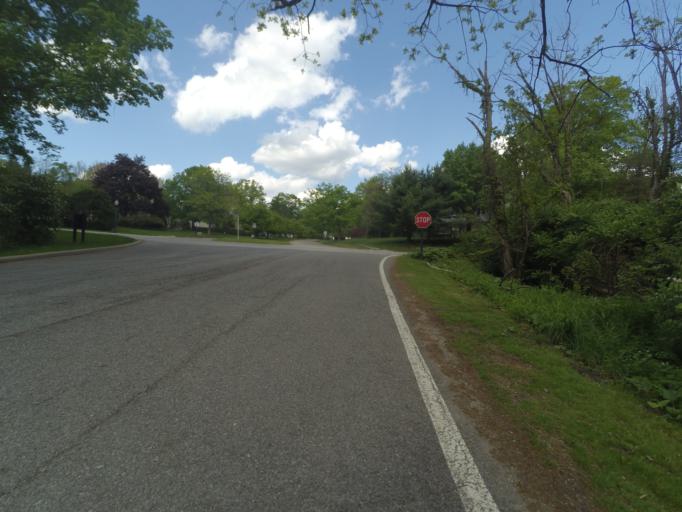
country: US
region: Ohio
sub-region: Mahoning County
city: Boardman
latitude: 41.0525
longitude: -80.6706
